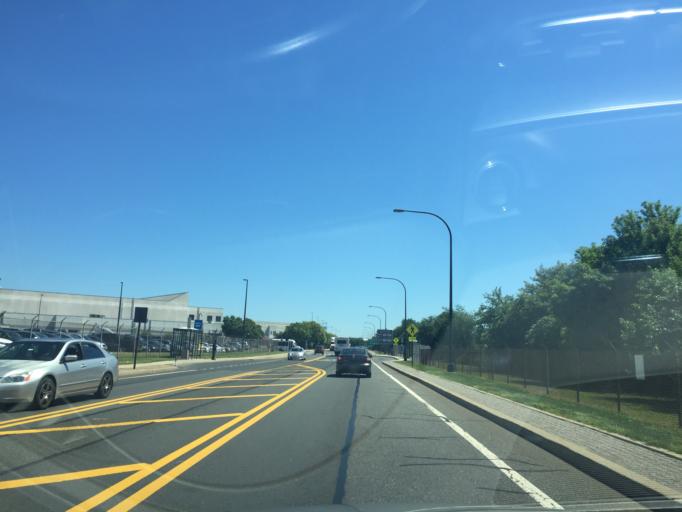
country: US
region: New Jersey
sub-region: Union County
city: Elizabeth
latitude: 40.6781
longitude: -74.1878
